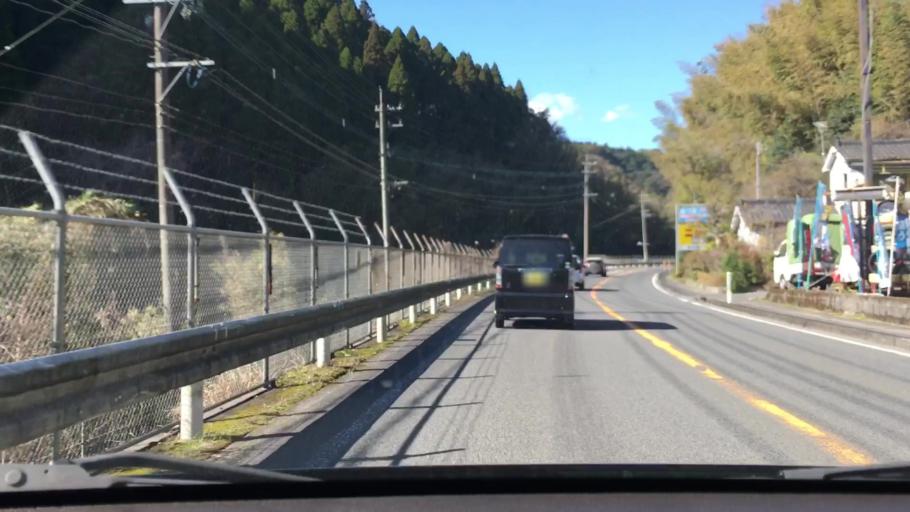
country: JP
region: Kagoshima
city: Ijuin
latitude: 31.6522
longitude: 130.5003
